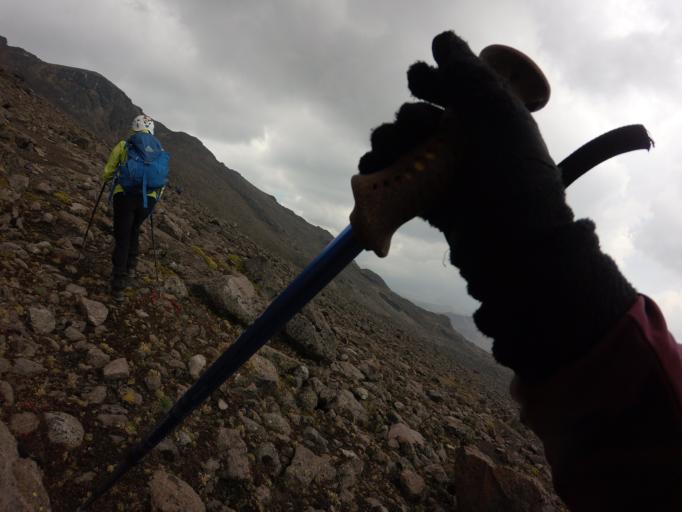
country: MX
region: Mexico
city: Amecameca de Juarez
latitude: 19.1579
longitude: -98.6439
